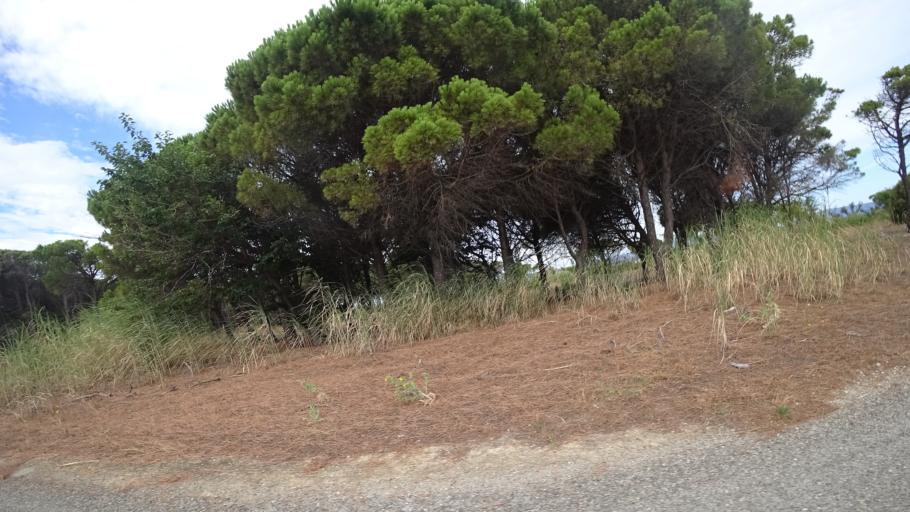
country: FR
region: Languedoc-Roussillon
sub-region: Departement de l'Aude
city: Leucate
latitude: 42.8725
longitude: 3.0374
